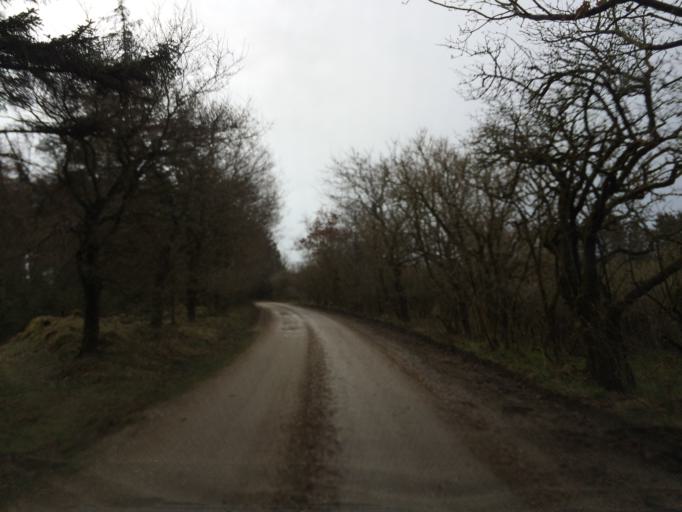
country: DK
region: Central Jutland
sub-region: Holstebro Kommune
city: Ulfborg
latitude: 56.2390
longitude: 8.4658
